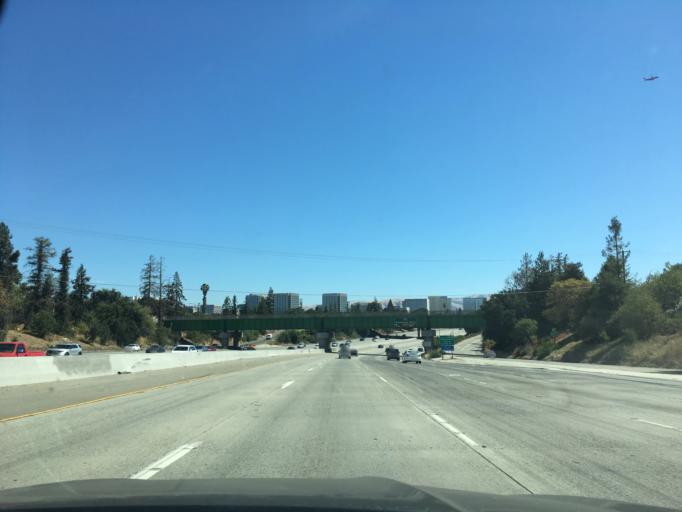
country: US
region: California
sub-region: Santa Clara County
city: Buena Vista
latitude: 37.3196
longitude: -121.9014
